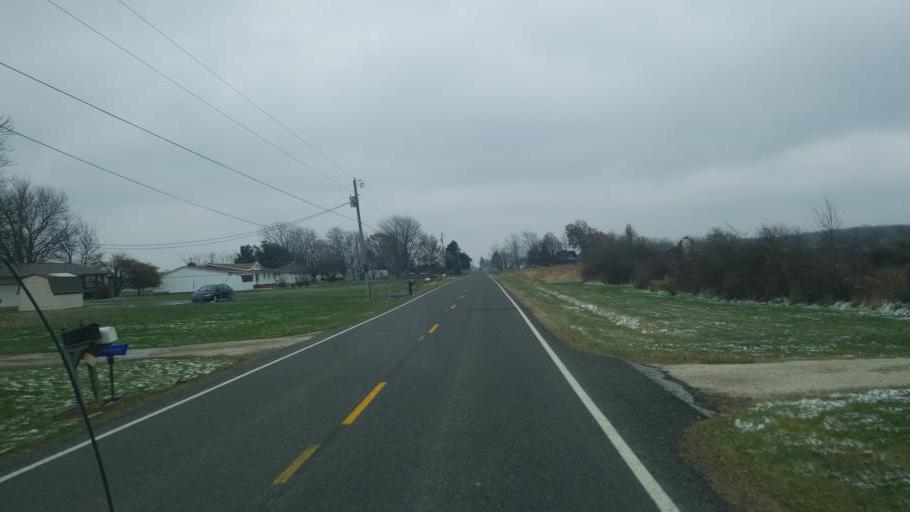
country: US
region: Ohio
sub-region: Medina County
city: Lodi
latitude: 41.1359
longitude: -81.9939
